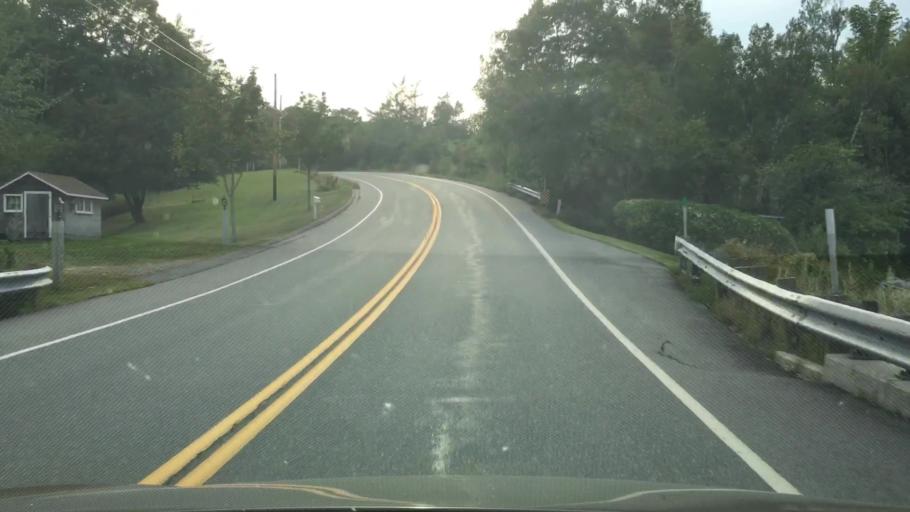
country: US
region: Maine
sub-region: Hancock County
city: Castine
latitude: 44.4470
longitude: -68.7837
